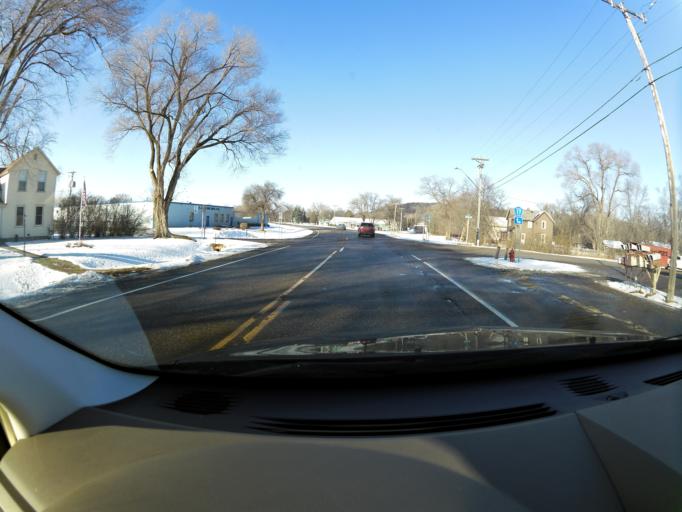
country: US
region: Minnesota
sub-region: Goodhue County
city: Cannon Falls
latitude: 44.5186
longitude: -92.9070
